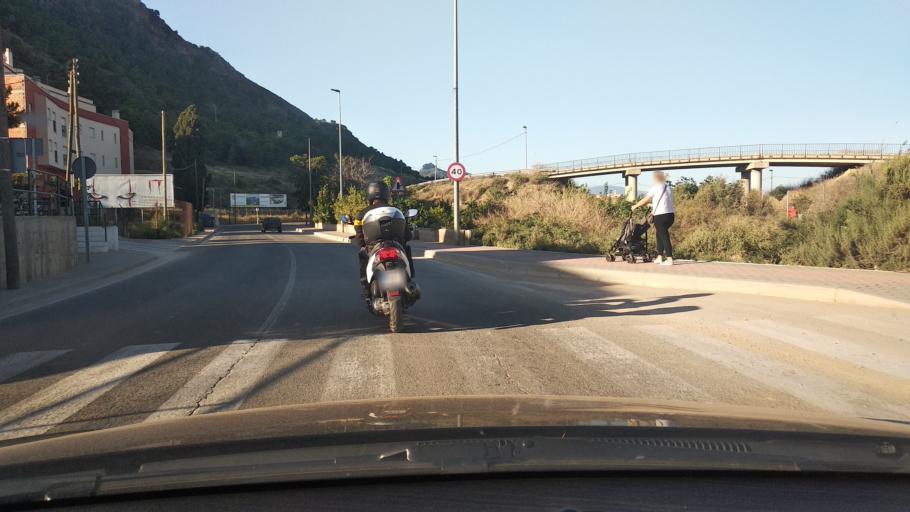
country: ES
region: Murcia
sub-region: Murcia
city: Beniel
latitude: 37.9888
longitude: -1.0420
